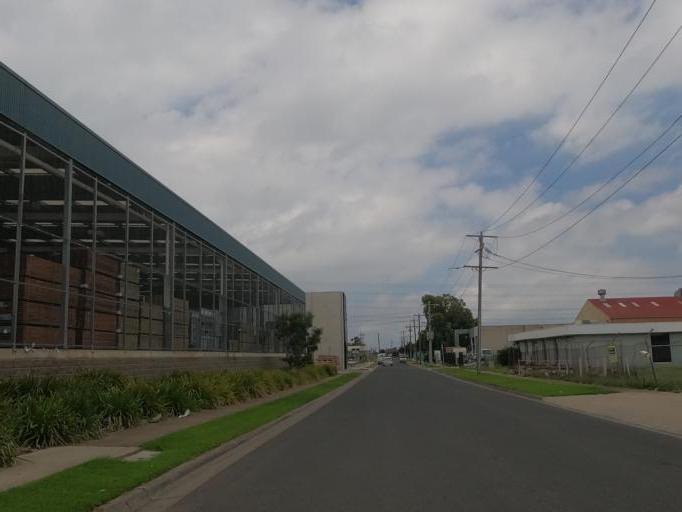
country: AU
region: Victoria
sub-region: Whittlesea
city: Thomastown
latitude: -37.6926
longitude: 145.0215
